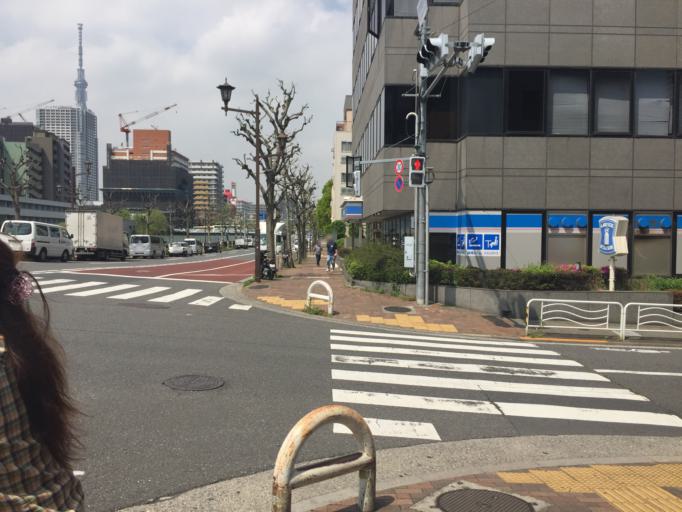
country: JP
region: Tokyo
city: Urayasu
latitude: 35.6940
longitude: 139.8201
